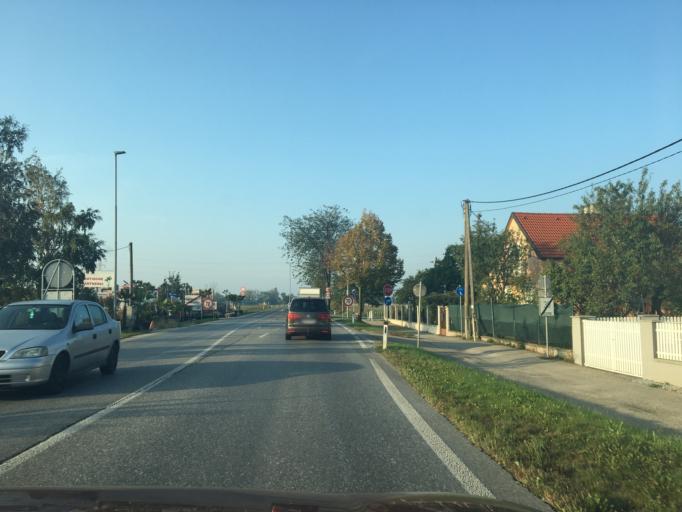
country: AT
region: Lower Austria
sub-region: Politischer Bezirk Wien-Umgebung
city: Gerasdorf bei Wien
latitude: 48.3177
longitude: 16.4375
